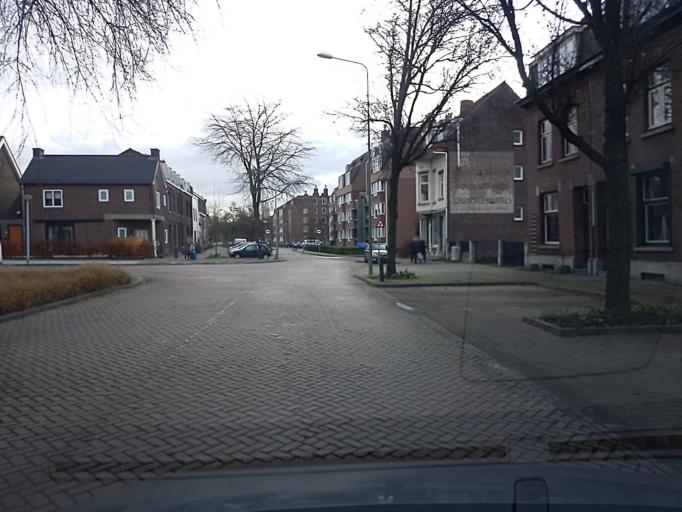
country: NL
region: Limburg
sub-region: Gemeente Maastricht
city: Maastricht
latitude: 50.8457
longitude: 5.7092
